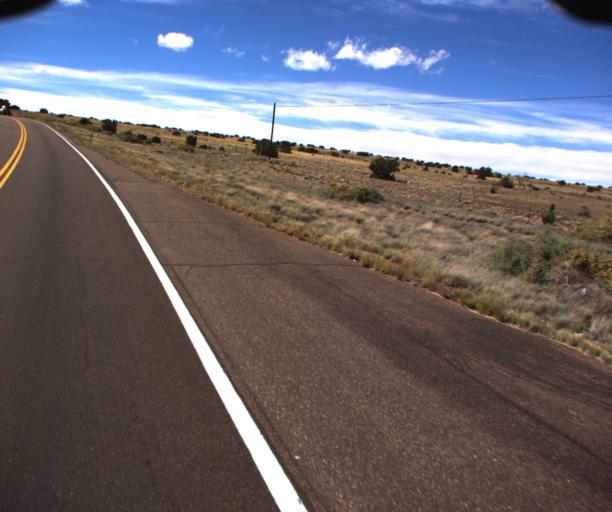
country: US
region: Arizona
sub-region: Apache County
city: Saint Johns
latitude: 34.4997
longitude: -109.4974
